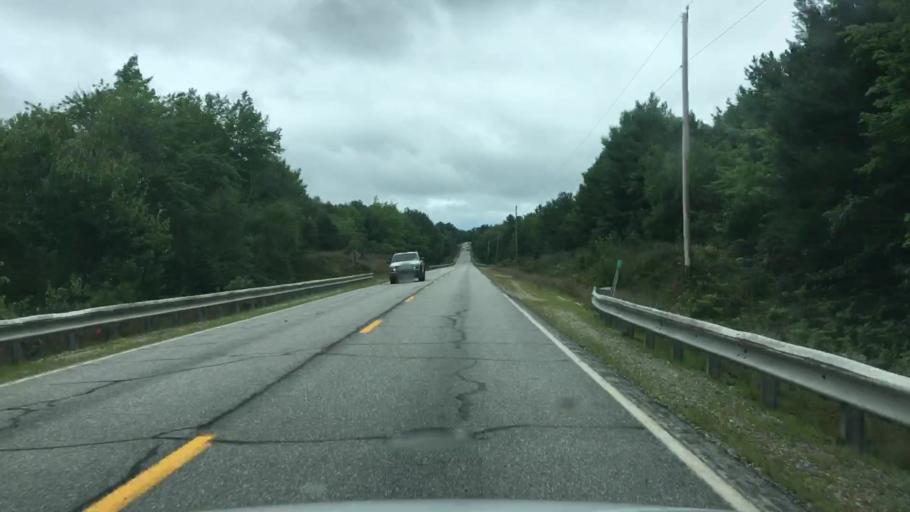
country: US
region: Maine
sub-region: Oxford County
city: Brownfield
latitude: 43.9209
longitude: -70.8612
